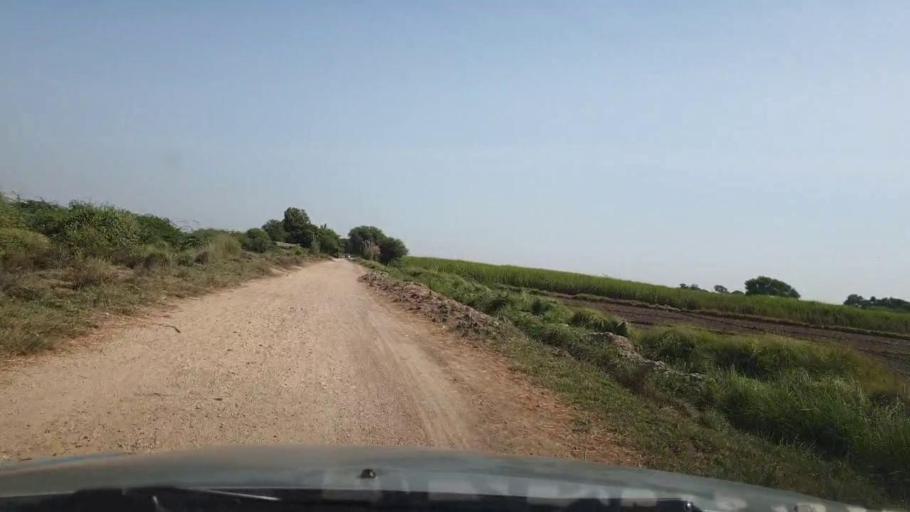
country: PK
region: Sindh
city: Bulri
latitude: 25.0179
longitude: 68.3134
